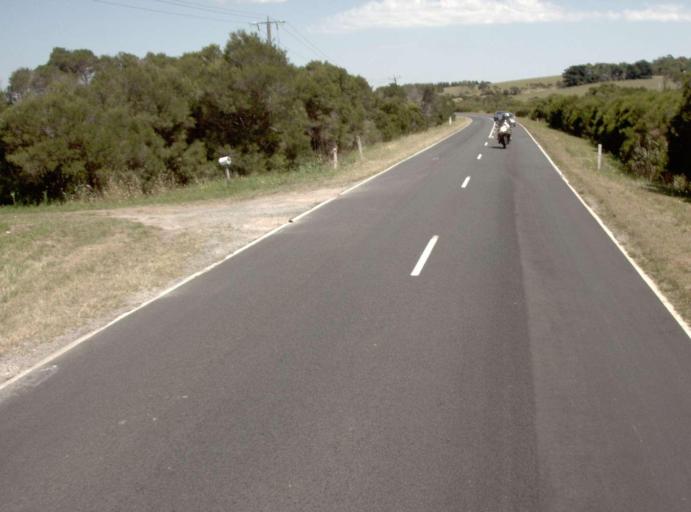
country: AU
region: Victoria
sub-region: Bass Coast
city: North Wonthaggi
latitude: -38.6284
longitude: 145.8236
